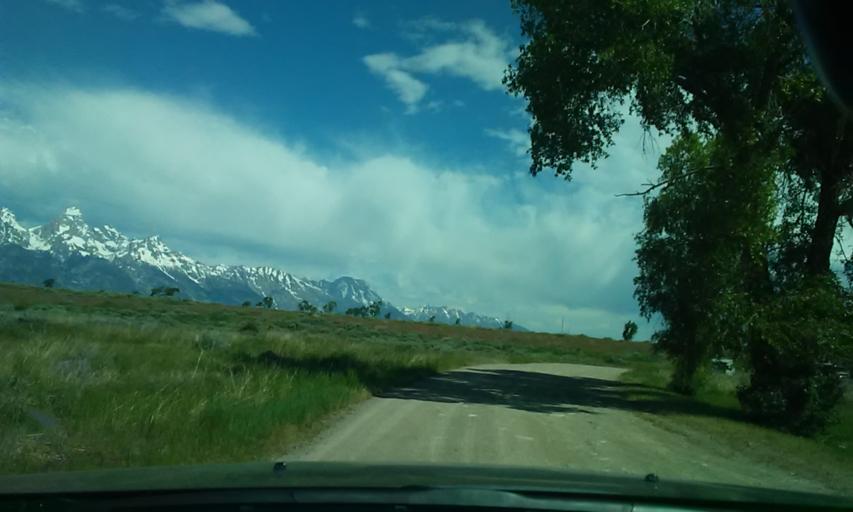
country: US
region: Wyoming
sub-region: Teton County
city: Jackson
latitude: 43.6217
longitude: -110.6289
